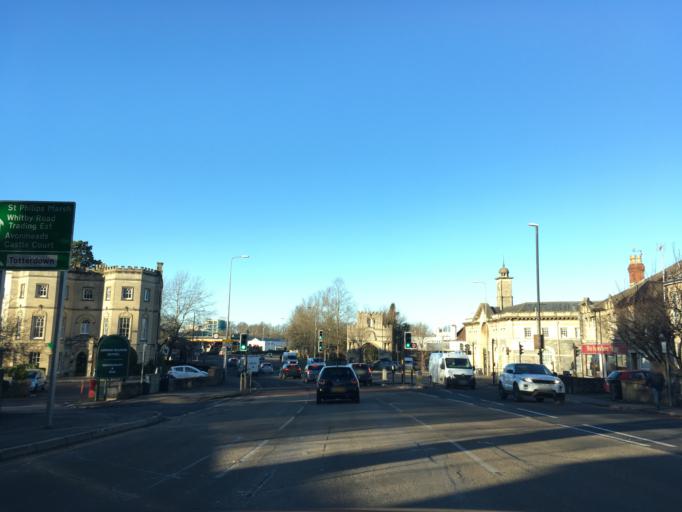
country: GB
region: England
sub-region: Bath and North East Somerset
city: Whitchurch
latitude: 51.4409
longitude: -2.5597
